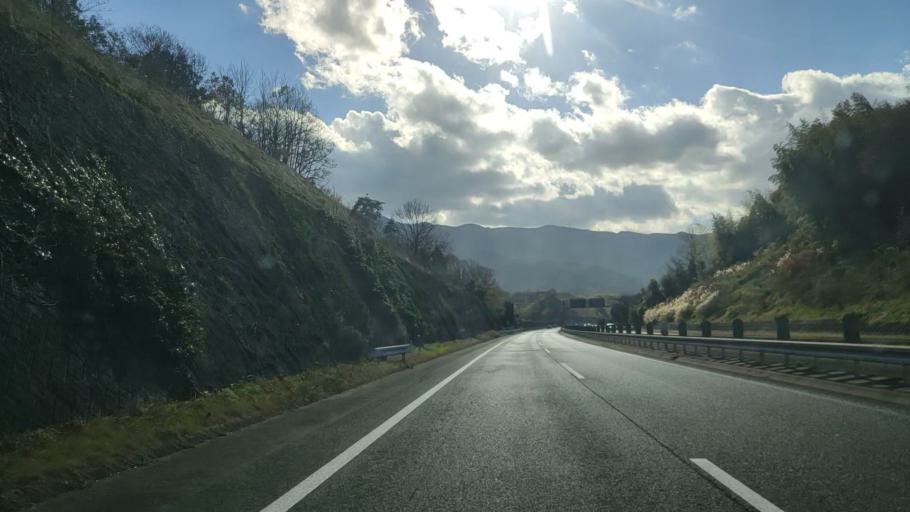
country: JP
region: Ehime
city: Kawanoecho
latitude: 33.9943
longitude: 133.5954
